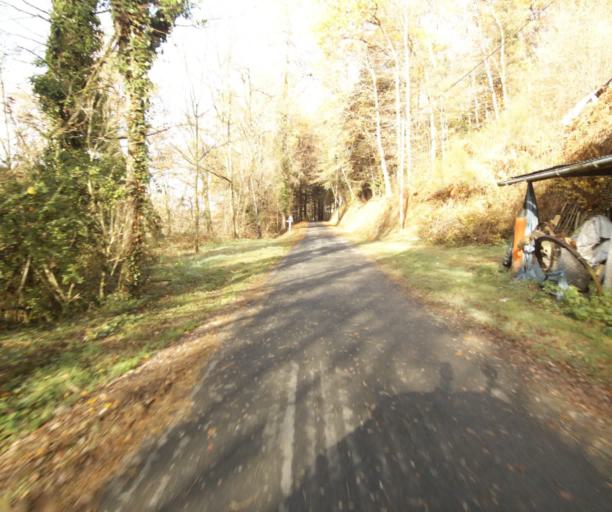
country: FR
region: Limousin
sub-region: Departement de la Correze
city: Sainte-Fortunade
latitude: 45.2161
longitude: 1.7470
